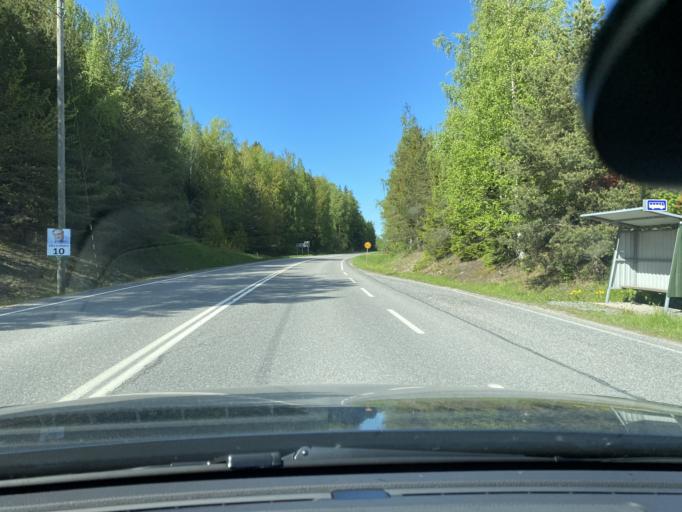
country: FI
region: Varsinais-Suomi
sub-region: Turku
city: Sauvo
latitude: 60.3563
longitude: 22.6693
